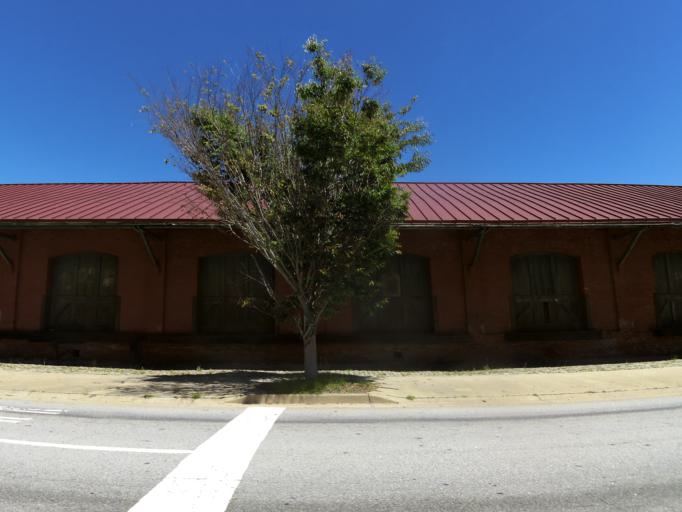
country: US
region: Georgia
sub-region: Richmond County
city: Augusta
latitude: 33.4749
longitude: -81.9599
